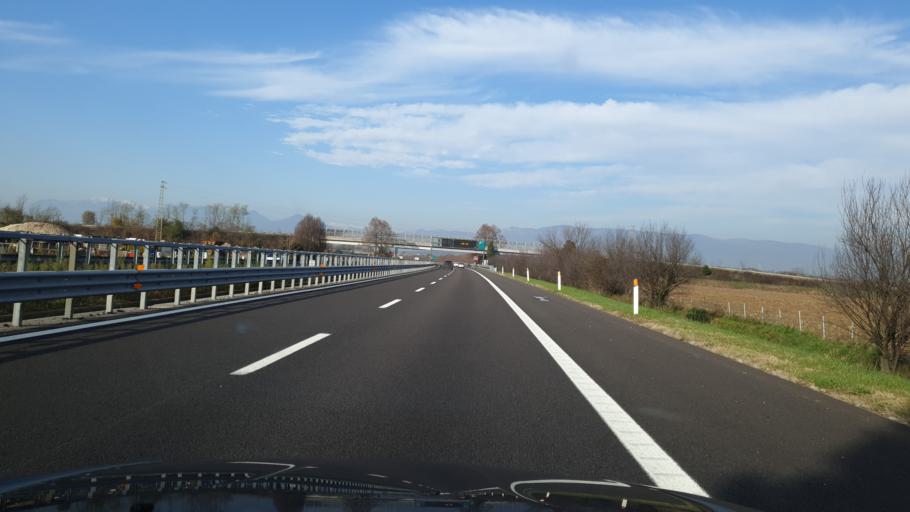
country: IT
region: Veneto
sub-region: Provincia di Vicenza
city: Vigardolo
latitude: 45.6236
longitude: 11.5944
